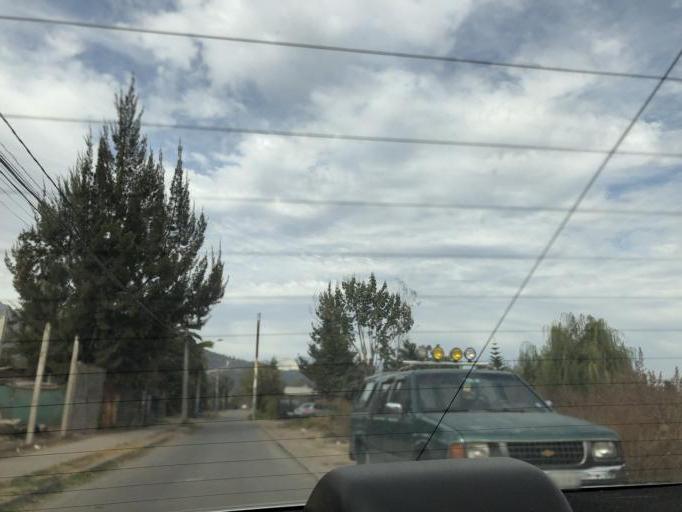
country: CL
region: Santiago Metropolitan
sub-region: Provincia de Cordillera
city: Puente Alto
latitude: -33.6099
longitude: -70.5377
